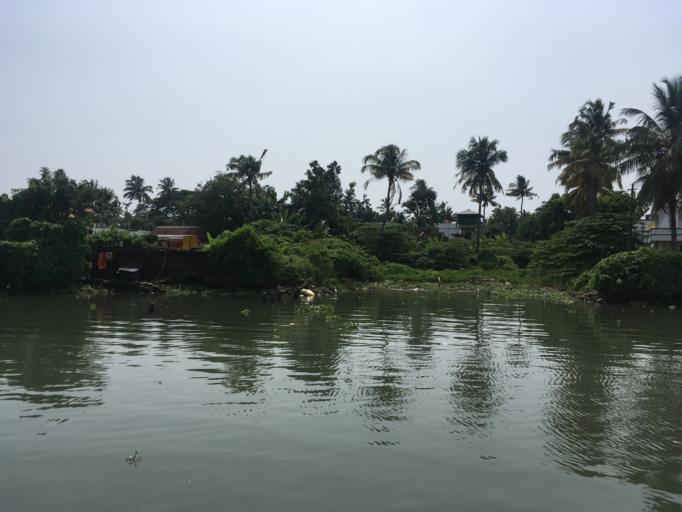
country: IN
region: Kerala
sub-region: Ernakulam
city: Cochin
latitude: 9.9773
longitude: 76.2430
